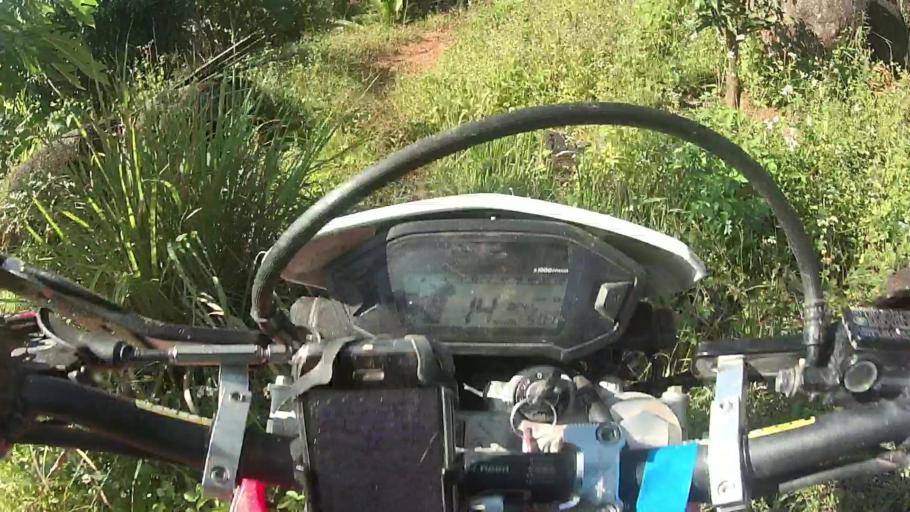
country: TH
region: Chiang Mai
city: Phrao
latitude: 19.4098
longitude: 99.2948
